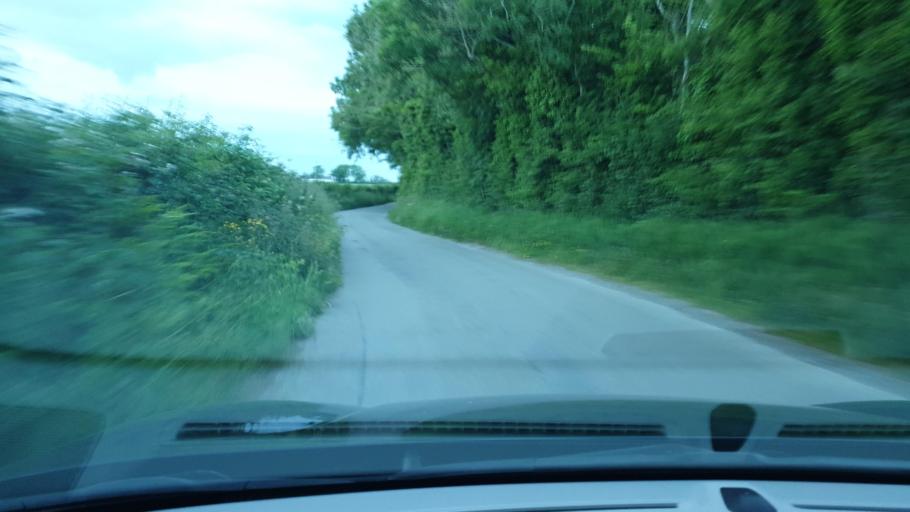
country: IE
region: Leinster
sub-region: An Mhi
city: Ashbourne
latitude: 53.5449
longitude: -6.3529
